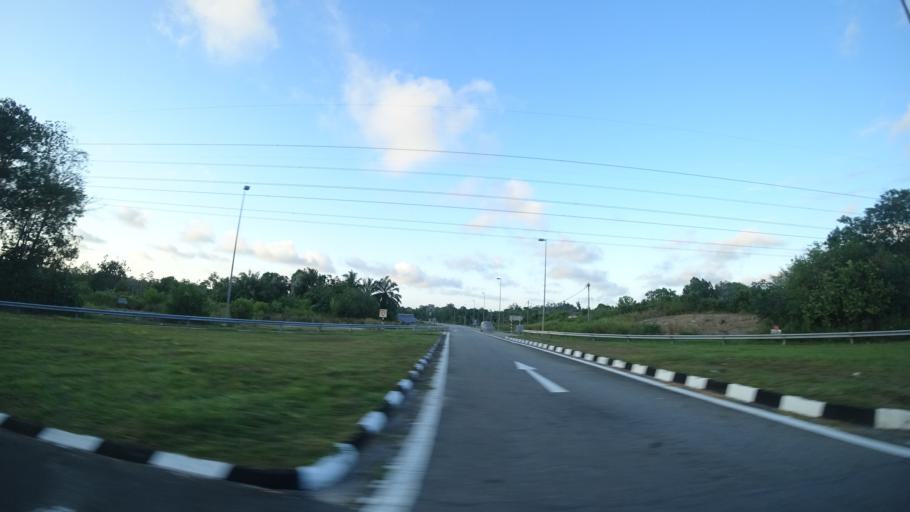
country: BN
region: Tutong
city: Tutong
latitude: 4.8306
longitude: 114.7193
